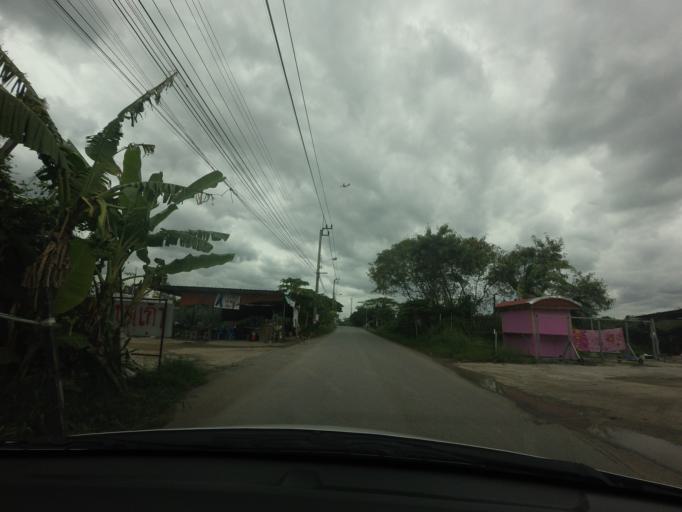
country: TH
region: Bangkok
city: Lat Krabang
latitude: 13.7755
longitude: 100.7702
